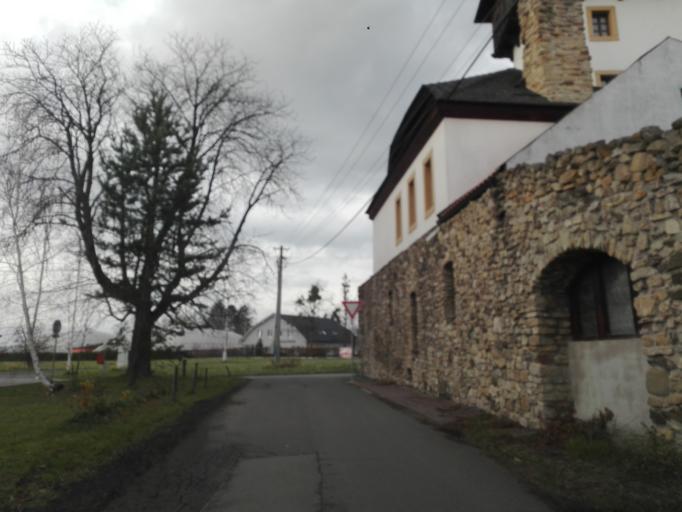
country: CZ
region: Moravskoslezsky
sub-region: Okres Frydek-Mistek
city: Frydek-Mistek
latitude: 49.6973
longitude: 18.3502
